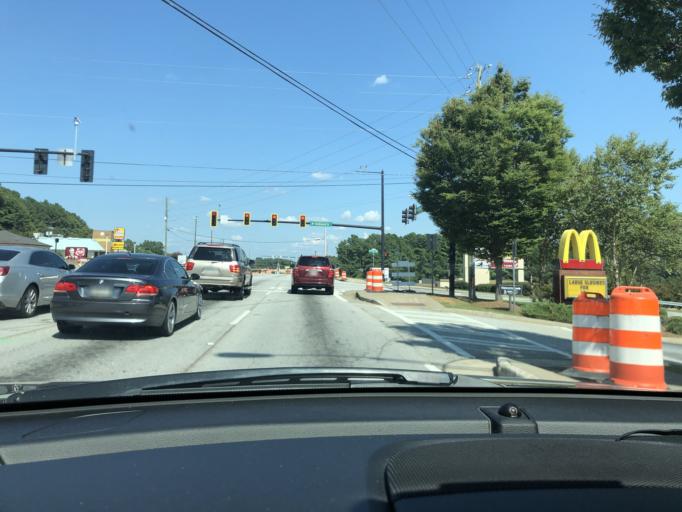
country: US
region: Georgia
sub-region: Gwinnett County
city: Snellville
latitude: 33.8559
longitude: -84.0254
